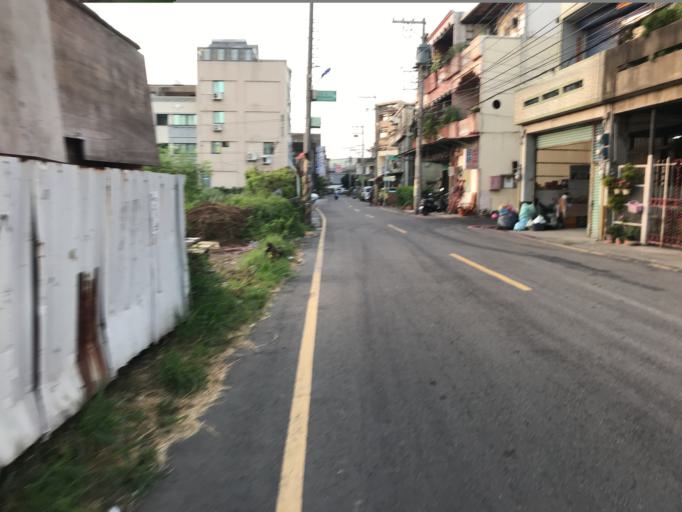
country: TW
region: Taiwan
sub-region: Hsinchu
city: Hsinchu
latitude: 24.8041
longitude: 120.9386
